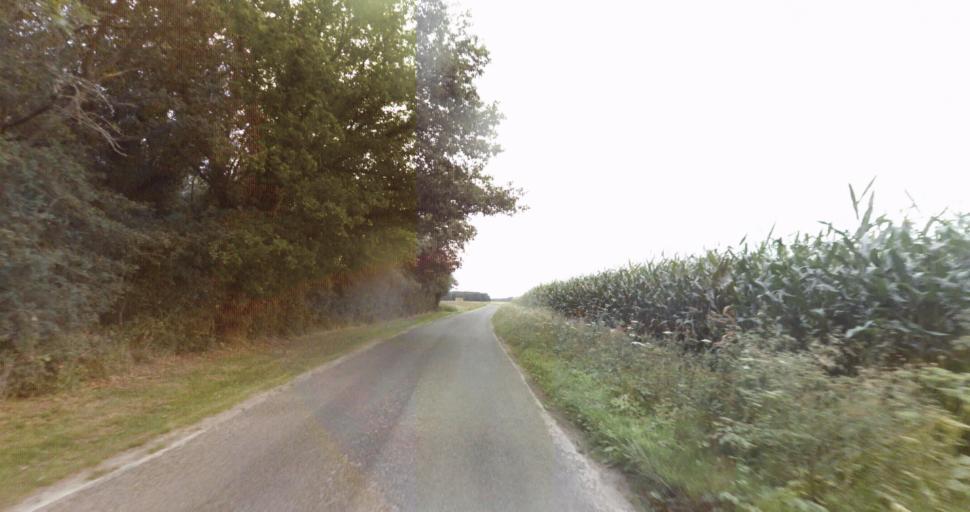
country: FR
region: Haute-Normandie
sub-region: Departement de l'Eure
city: Marcilly-sur-Eure
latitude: 48.8628
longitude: 1.3245
